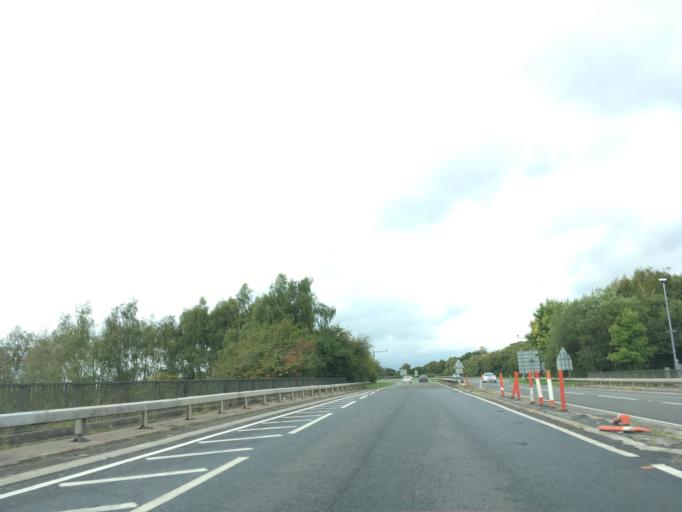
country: GB
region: Wales
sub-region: Monmouthshire
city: Llanarth
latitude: 51.7672
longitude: -2.8337
